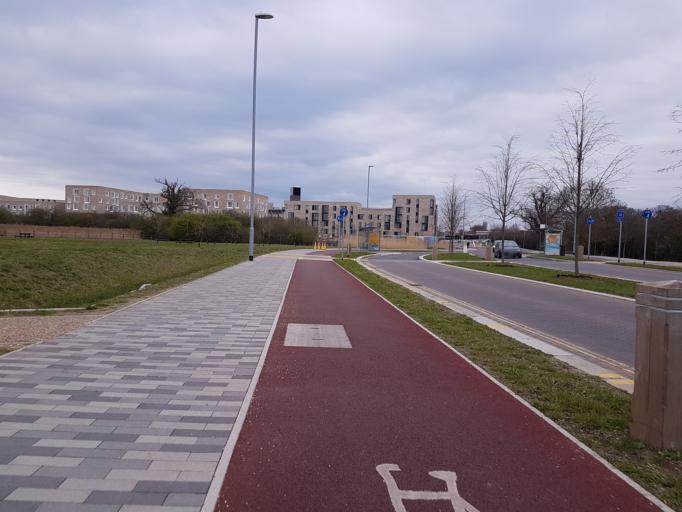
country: GB
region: England
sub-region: Cambridgeshire
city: Girton
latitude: 52.2149
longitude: 0.0860
